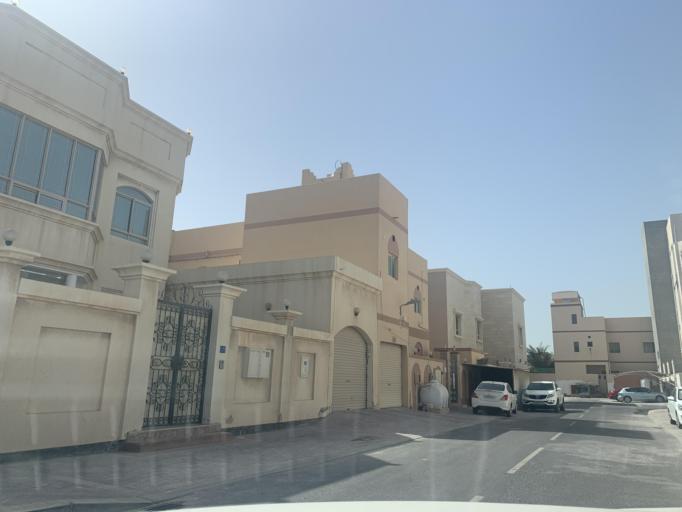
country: BH
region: Northern
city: Sitrah
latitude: 26.1663
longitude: 50.6269
